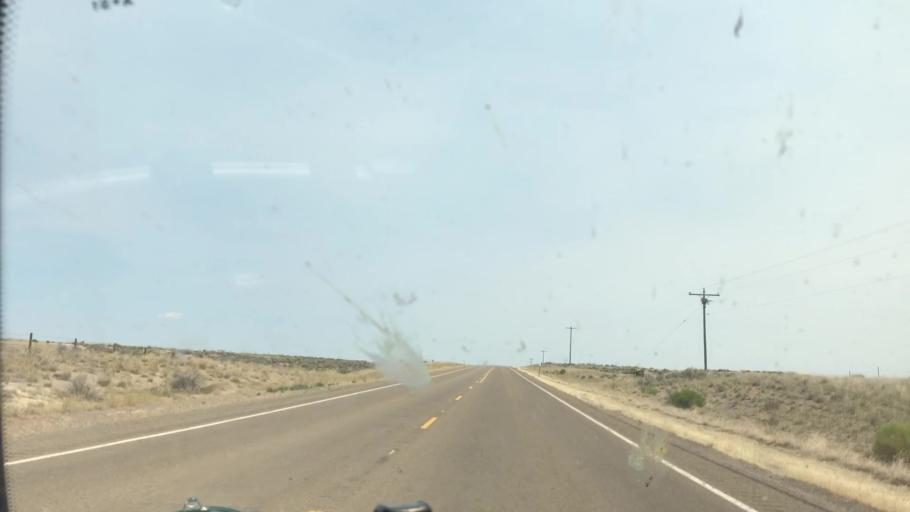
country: US
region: Idaho
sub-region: Owyhee County
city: Homedale
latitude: 42.8568
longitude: -117.5726
